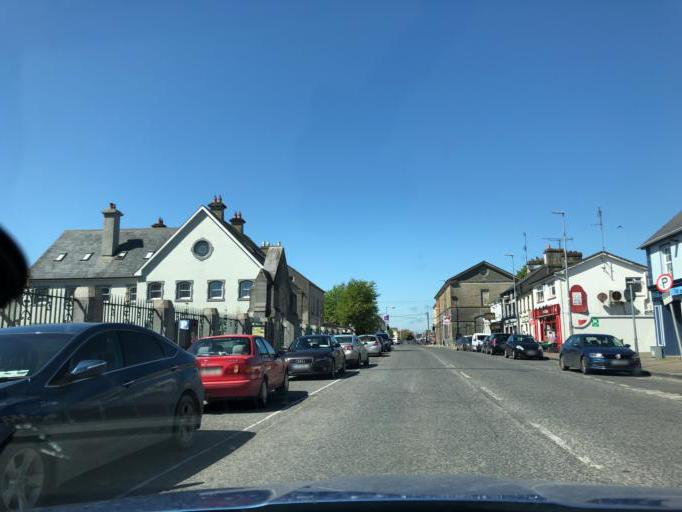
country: IE
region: Connaught
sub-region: County Galway
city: Loughrea
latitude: 53.1973
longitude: -8.5662
